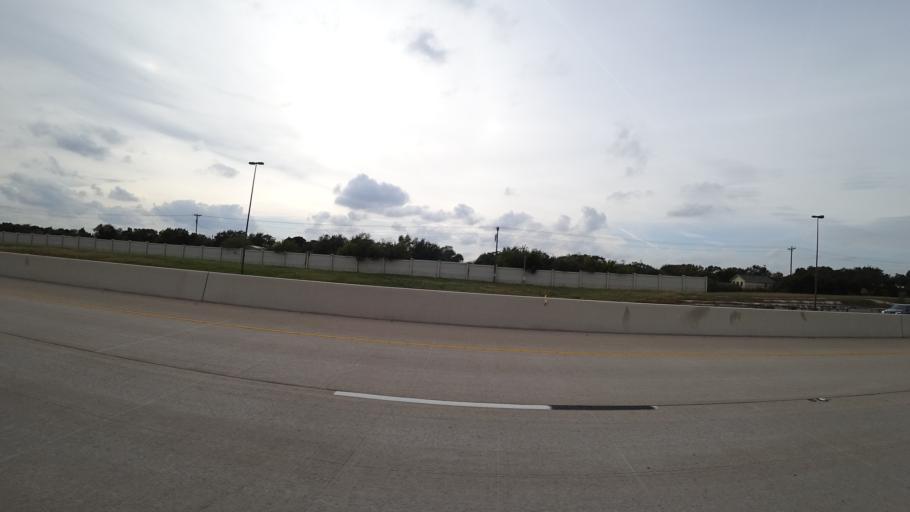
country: US
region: Texas
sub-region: Williamson County
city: Cedar Park
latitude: 30.5110
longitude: -97.8118
